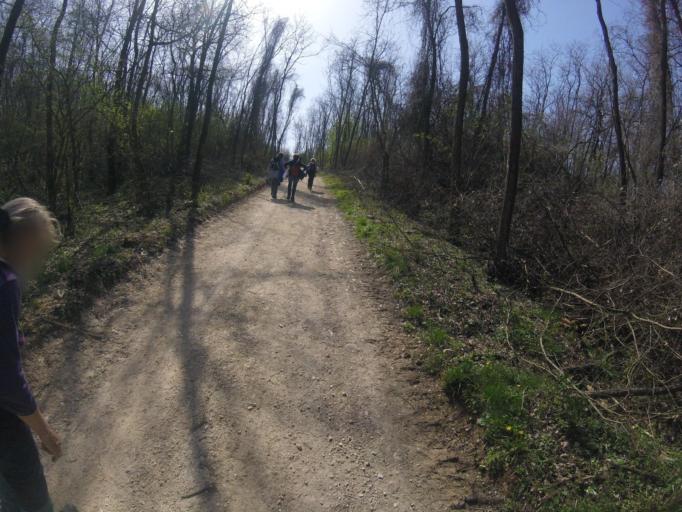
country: HU
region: Pest
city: Pilisszanto
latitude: 47.6590
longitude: 18.8698
